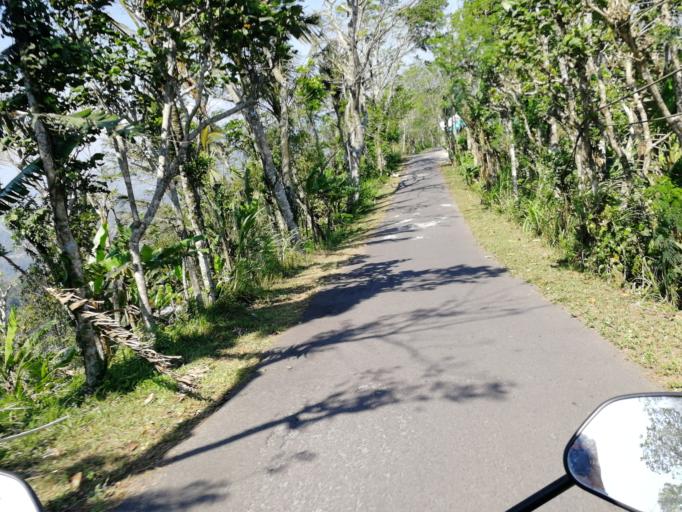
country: ID
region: Bali
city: Tiyingtali Kelod
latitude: -8.3920
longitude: 115.6361
